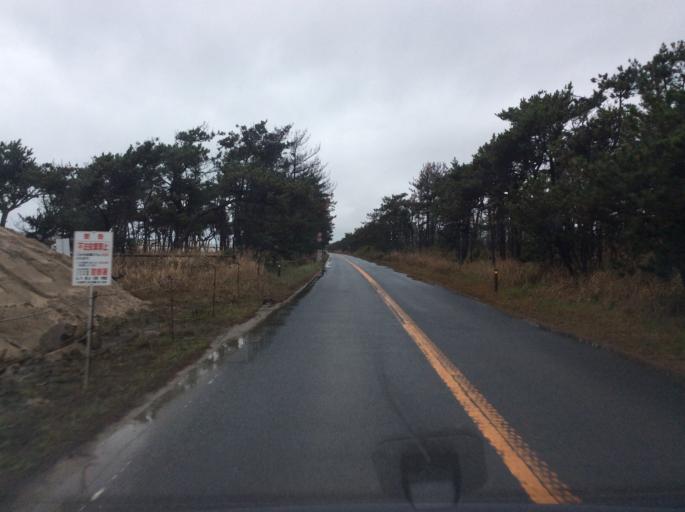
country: JP
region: Fukushima
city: Iwaki
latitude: 37.0723
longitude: 140.9773
